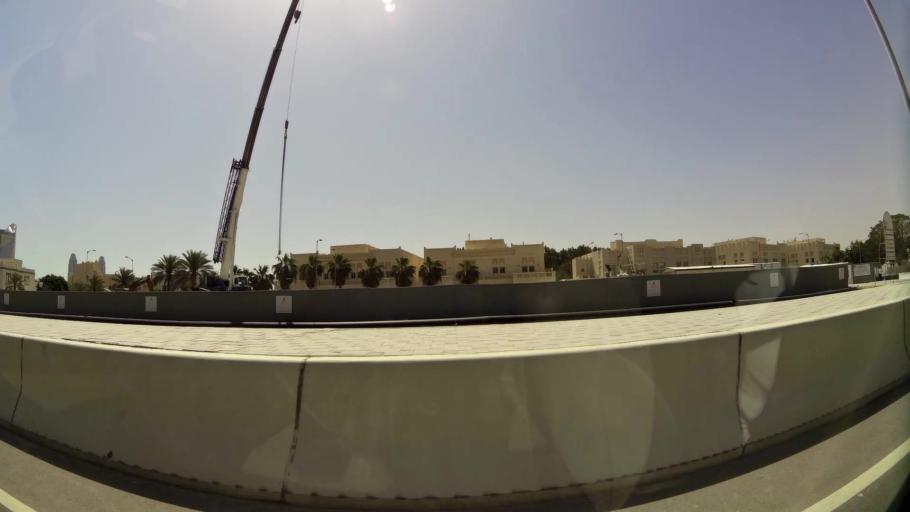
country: QA
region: Baladiyat ad Dawhah
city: Doha
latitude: 25.3789
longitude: 51.5139
